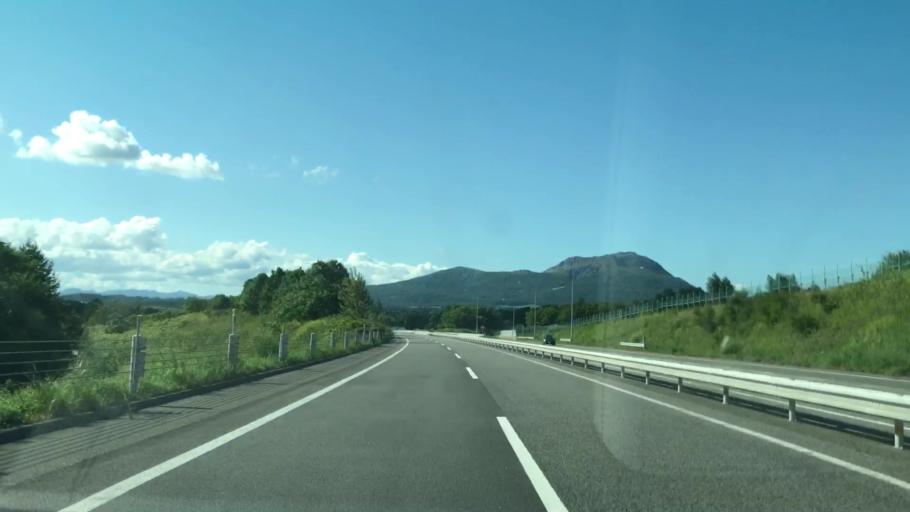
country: JP
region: Hokkaido
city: Date
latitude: 42.4828
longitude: 140.8958
